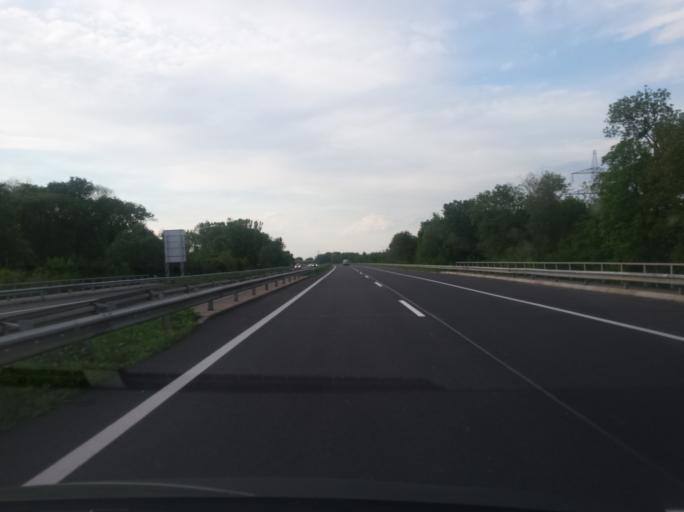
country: AT
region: Burgenland
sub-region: Eisenstadt-Umgebung
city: Wimpassing an der Leitha
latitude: 47.8985
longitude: 16.4140
